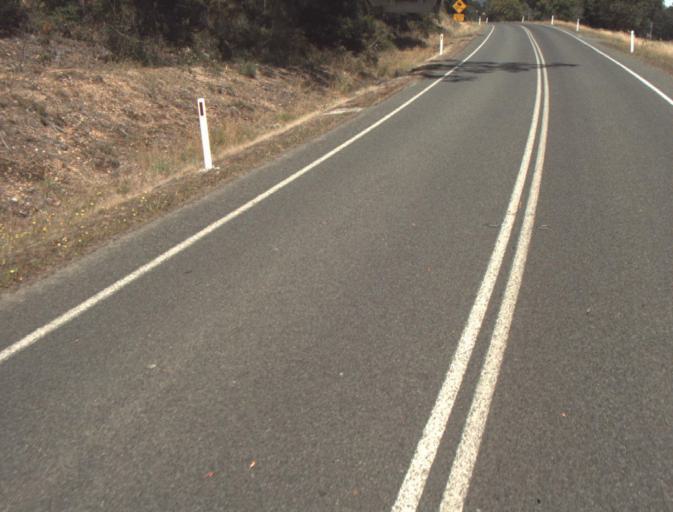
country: AU
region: Tasmania
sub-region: Dorset
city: Scottsdale
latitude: -41.3198
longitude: 147.3636
